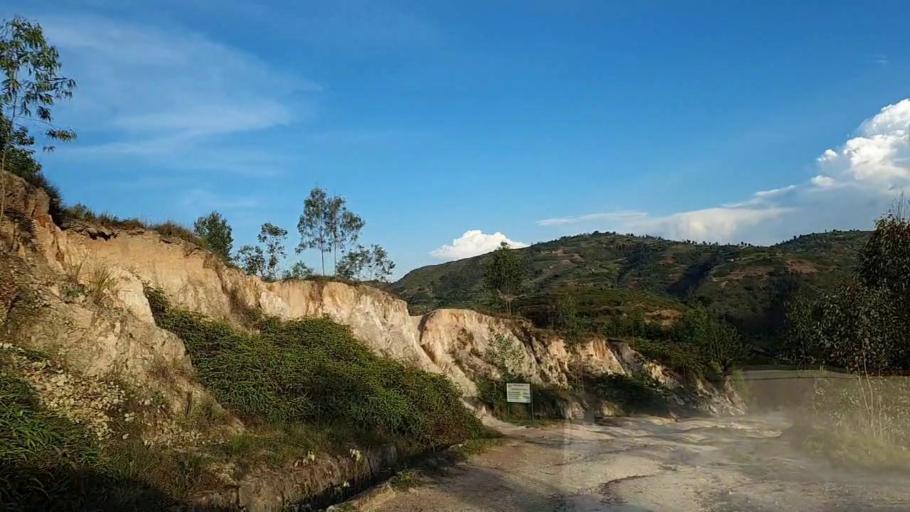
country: RW
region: Southern Province
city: Gikongoro
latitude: -2.3981
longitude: 29.5597
